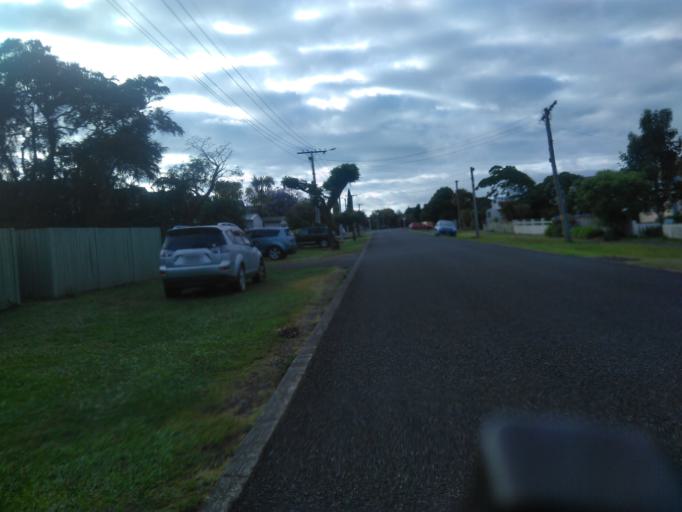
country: NZ
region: Gisborne
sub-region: Gisborne District
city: Gisborne
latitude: -38.6563
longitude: 178.0284
